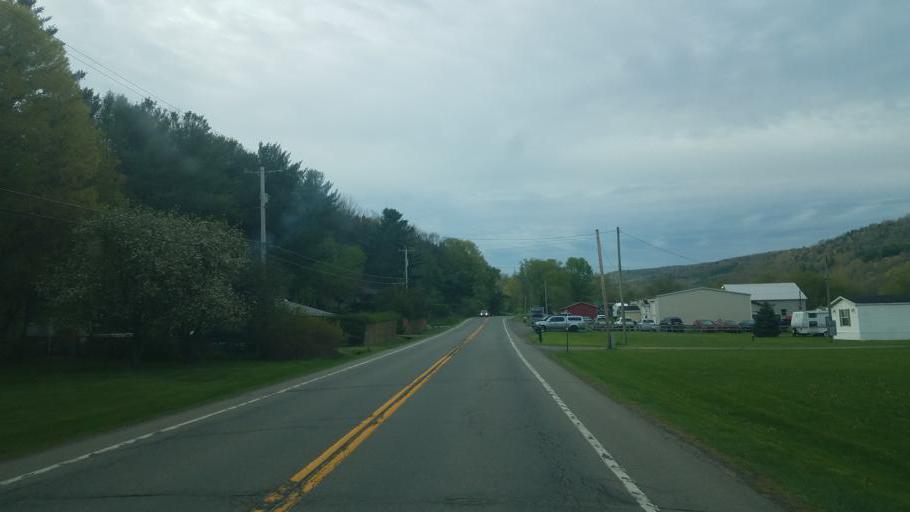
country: US
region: New York
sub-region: Steuben County
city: Canisteo
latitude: 42.2291
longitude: -77.5754
